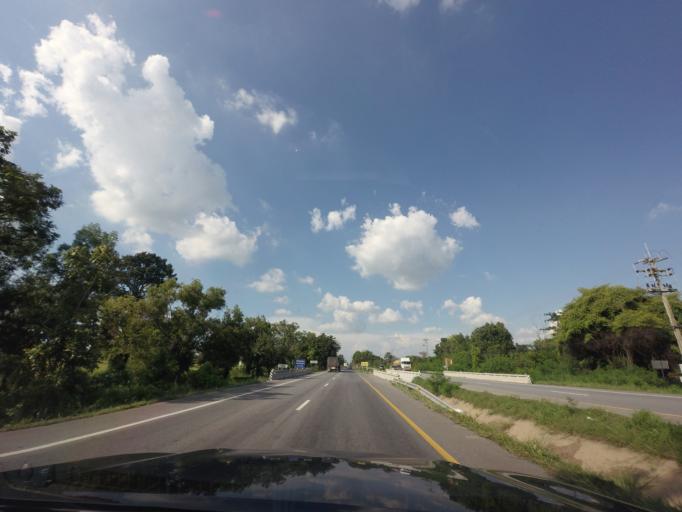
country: TH
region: Nakhon Ratchasima
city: Bua Lai
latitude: 15.7097
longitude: 102.5874
